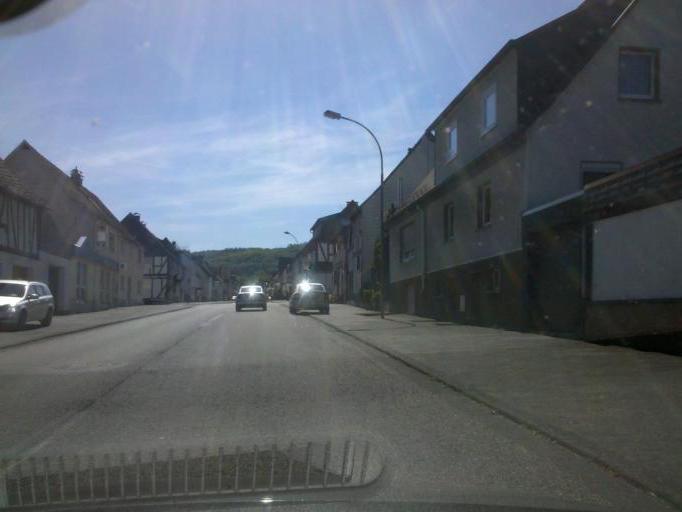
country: DE
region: Hesse
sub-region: Regierungsbezirk Giessen
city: Haiger
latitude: 50.7160
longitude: 8.1835
